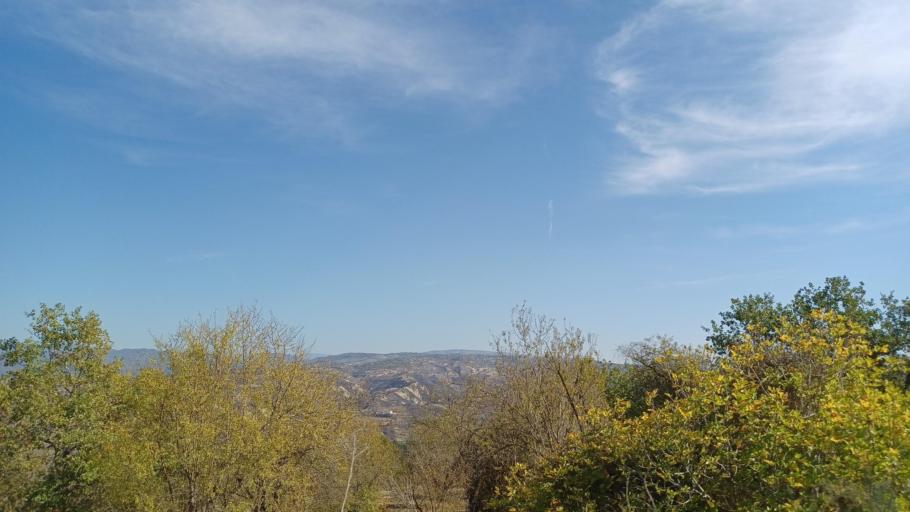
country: CY
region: Pafos
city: Pegeia
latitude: 34.9389
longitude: 32.4545
